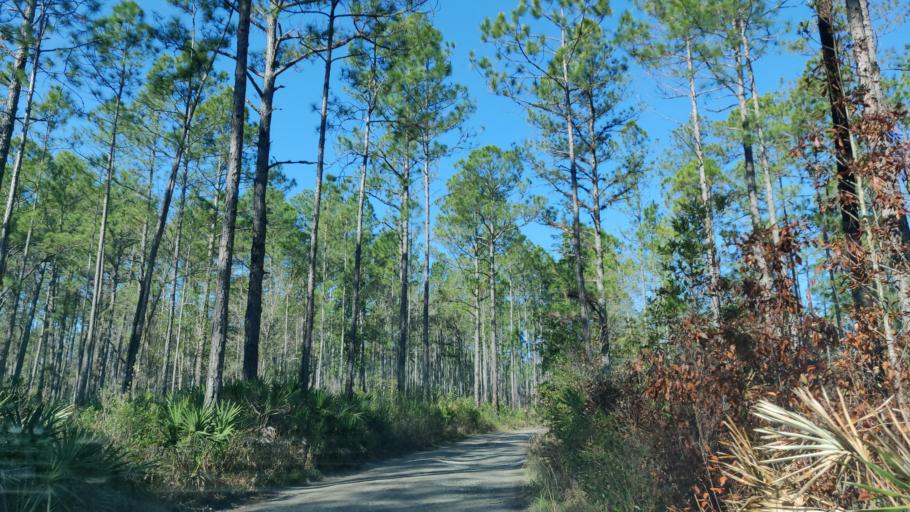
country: US
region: Florida
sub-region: Clay County
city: Middleburg
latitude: 30.1521
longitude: -81.9288
